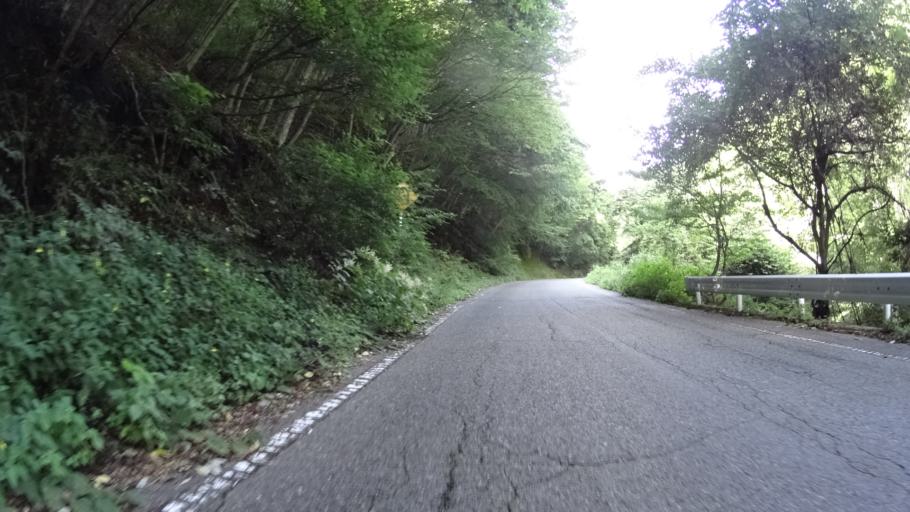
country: JP
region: Yamanashi
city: Nirasaki
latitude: 35.9081
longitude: 138.5397
